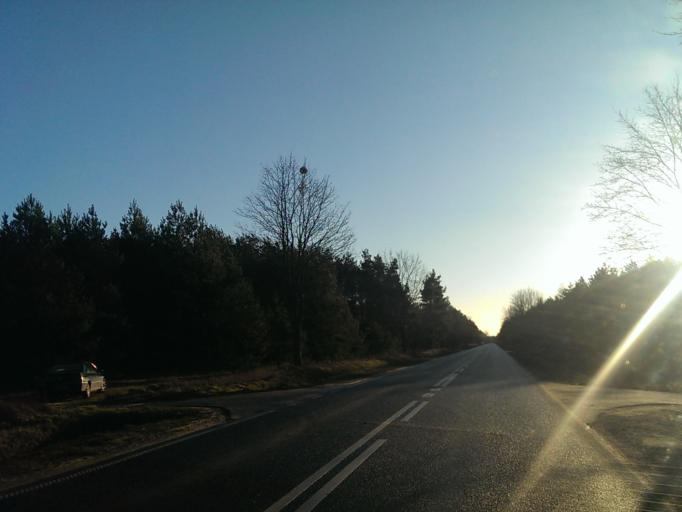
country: PL
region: Kujawsko-Pomorskie
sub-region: Powiat nakielski
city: Naklo nad Notecia
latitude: 53.0898
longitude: 17.5901
